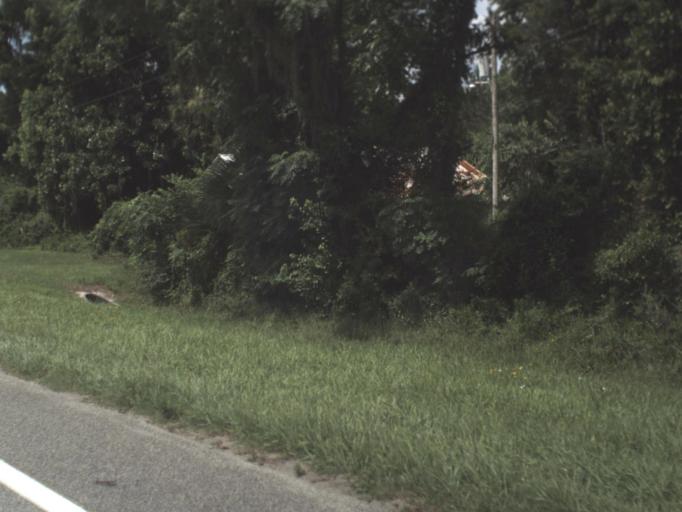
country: US
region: Florida
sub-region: Hamilton County
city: Jasper
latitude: 30.4118
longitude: -82.9337
